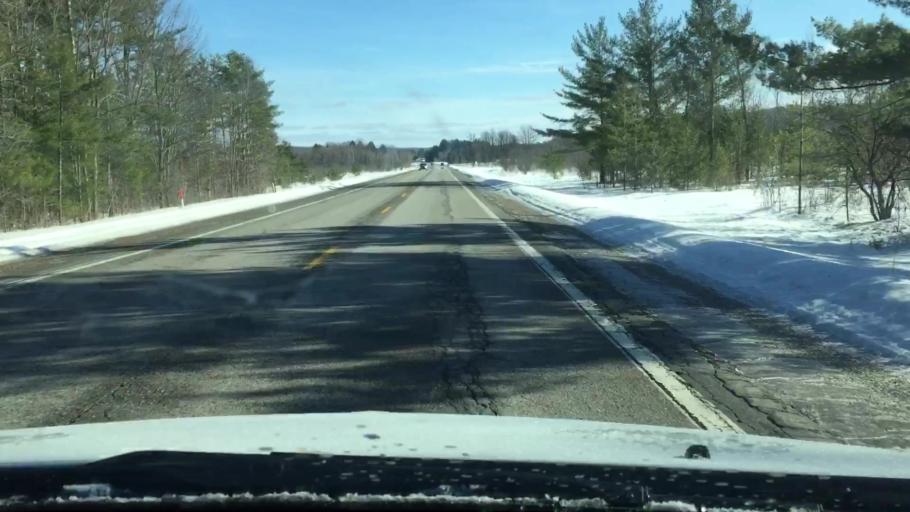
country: US
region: Michigan
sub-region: Charlevoix County
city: East Jordan
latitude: 45.1034
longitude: -85.1197
